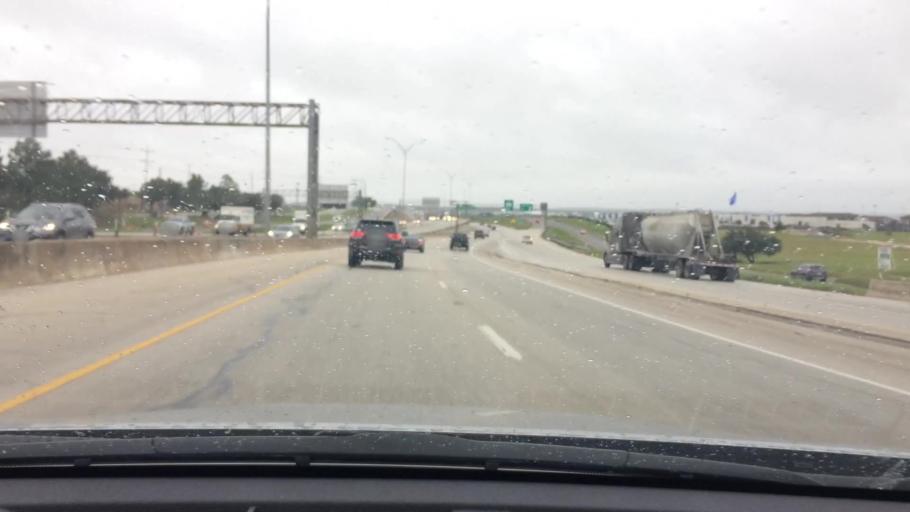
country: US
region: Texas
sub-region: Bexar County
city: Live Oak
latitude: 29.5704
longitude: -98.3356
